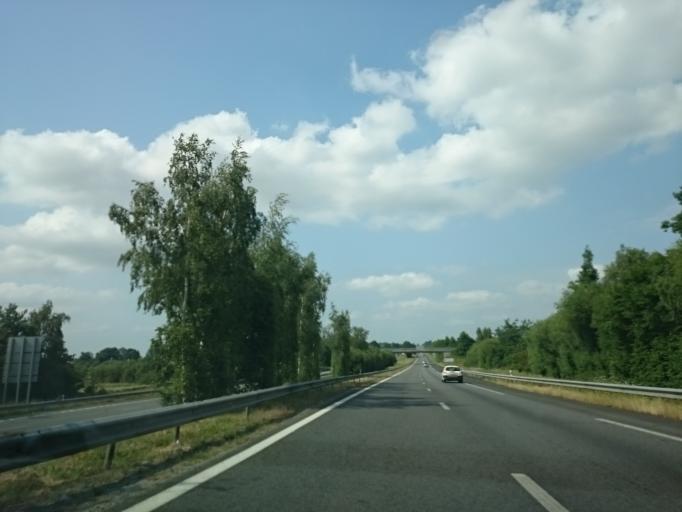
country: FR
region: Brittany
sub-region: Departement d'Ille-et-Vilaine
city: Bain-de-Bretagne
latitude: 47.8062
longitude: -1.6902
